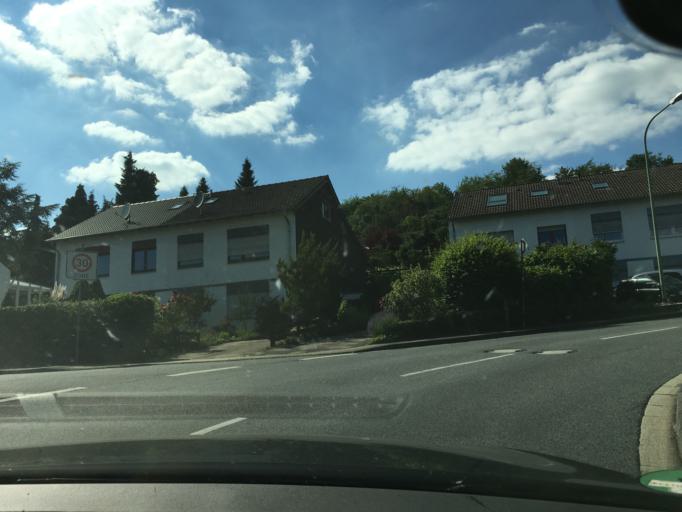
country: DE
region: North Rhine-Westphalia
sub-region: Regierungsbezirk Koln
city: Kreuzau
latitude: 50.7296
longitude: 6.4523
